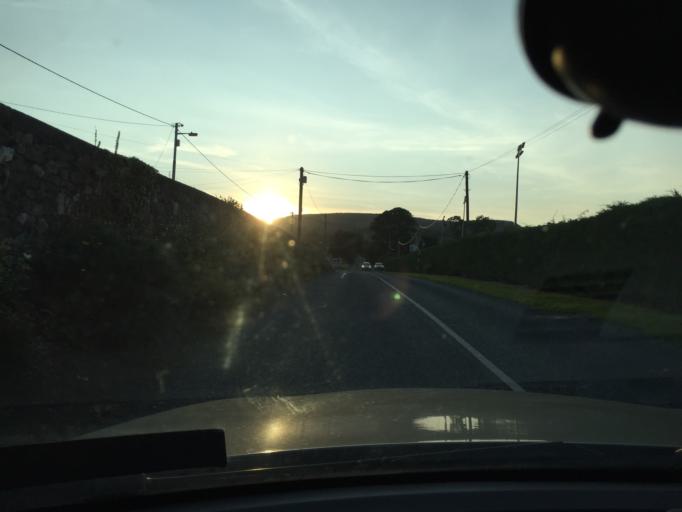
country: IE
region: Leinster
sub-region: Wicklow
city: Enniskerry
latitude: 53.1927
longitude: -6.1809
